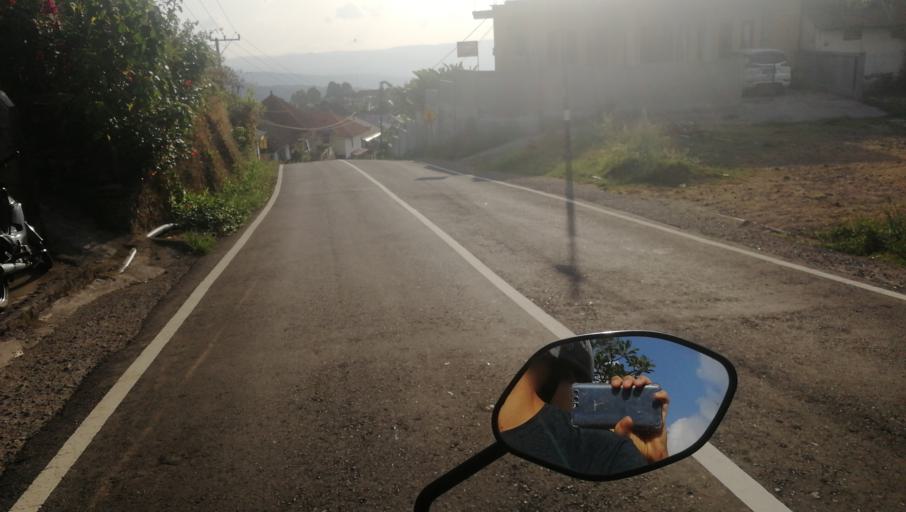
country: ID
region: Bali
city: Munduk
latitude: -8.2657
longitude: 115.0578
